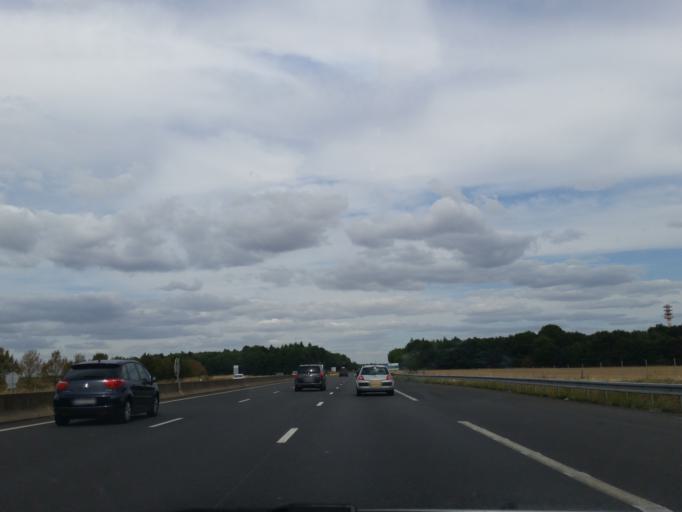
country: FR
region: Centre
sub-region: Departement d'Indre-et-Loire
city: Monnaie
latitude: 47.4787
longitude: 0.7845
